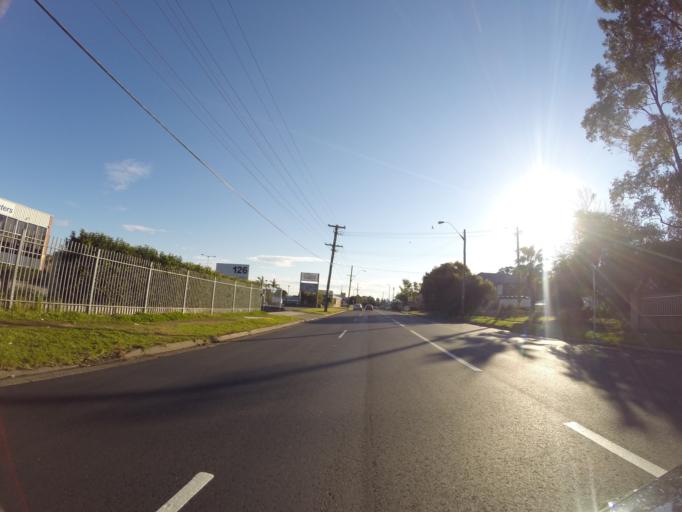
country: AU
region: New South Wales
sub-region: Fairfield
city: Fairfield East
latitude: -33.8688
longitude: 150.9725
